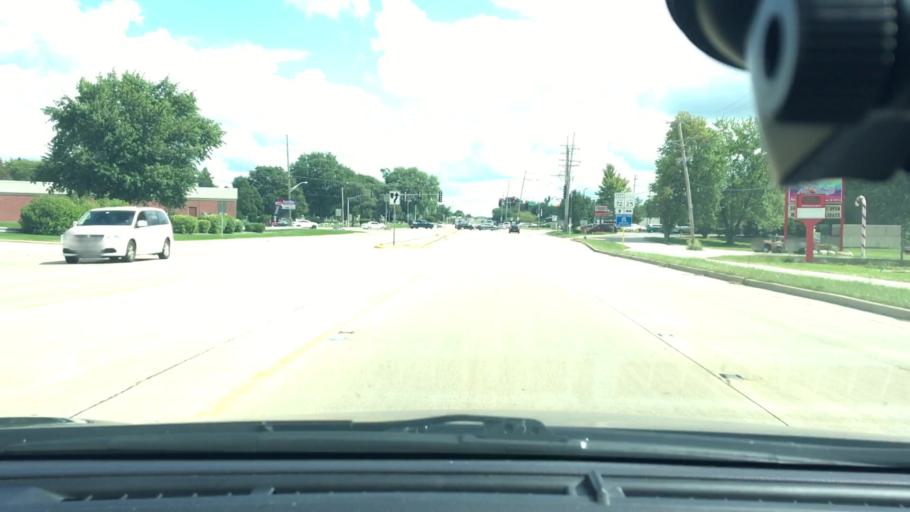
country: US
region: Illinois
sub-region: Kane County
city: East Dundee
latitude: 42.0943
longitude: -88.2603
